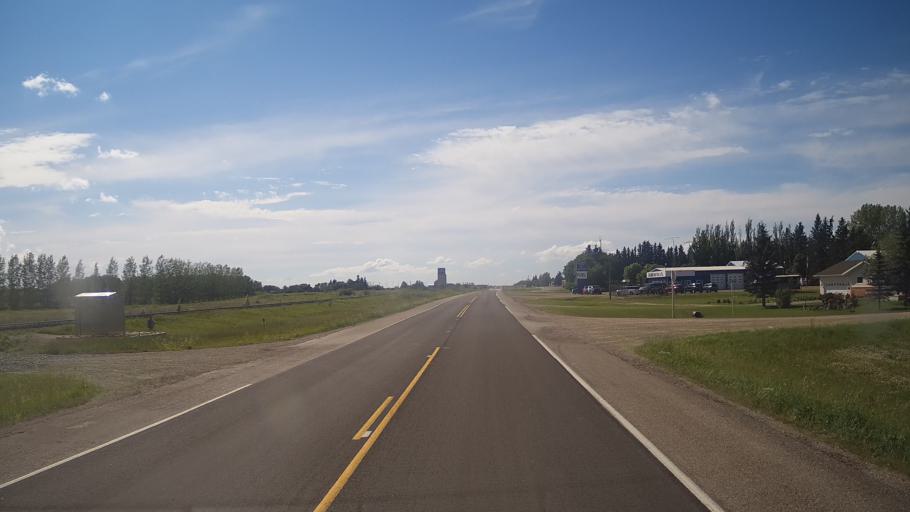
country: CA
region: Saskatchewan
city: Foam Lake
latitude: 51.2595
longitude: -103.7280
